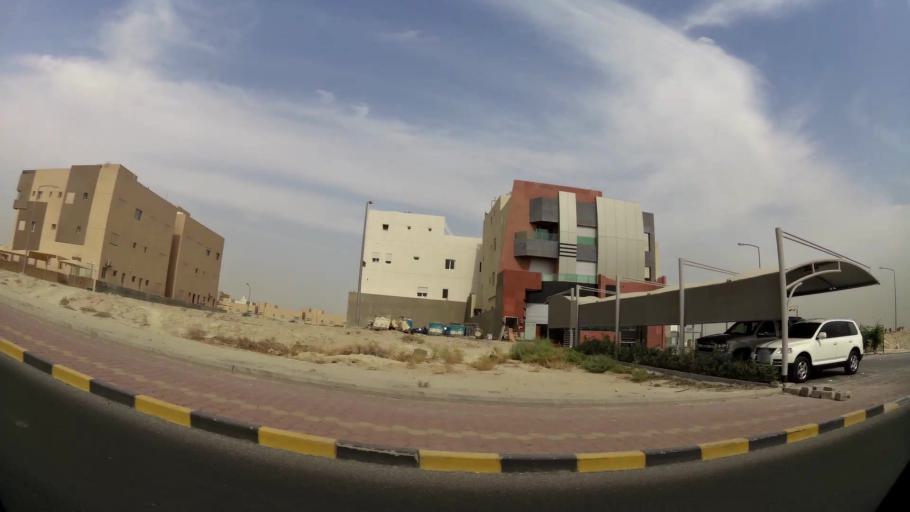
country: KW
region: Al Farwaniyah
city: Janub as Surrah
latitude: 29.2862
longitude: 47.9990
